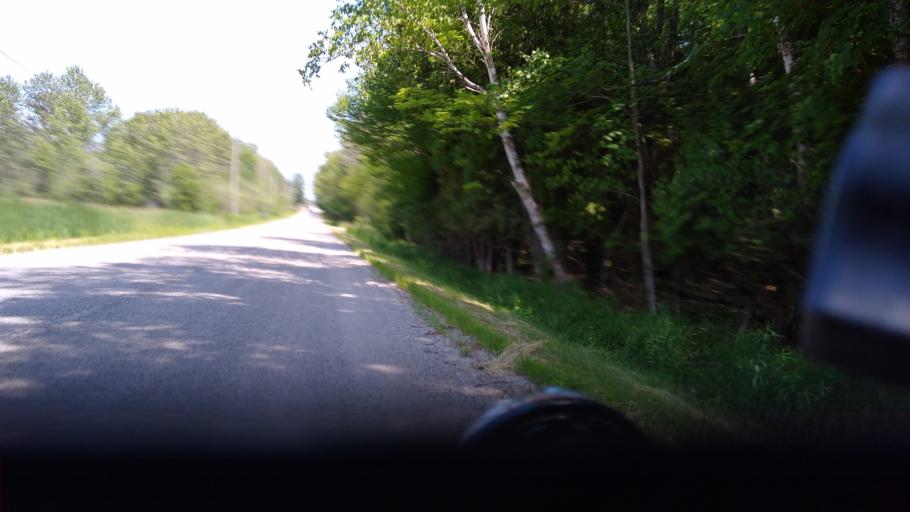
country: US
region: Michigan
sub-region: Delta County
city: Escanaba
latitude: 45.7101
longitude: -87.1381
